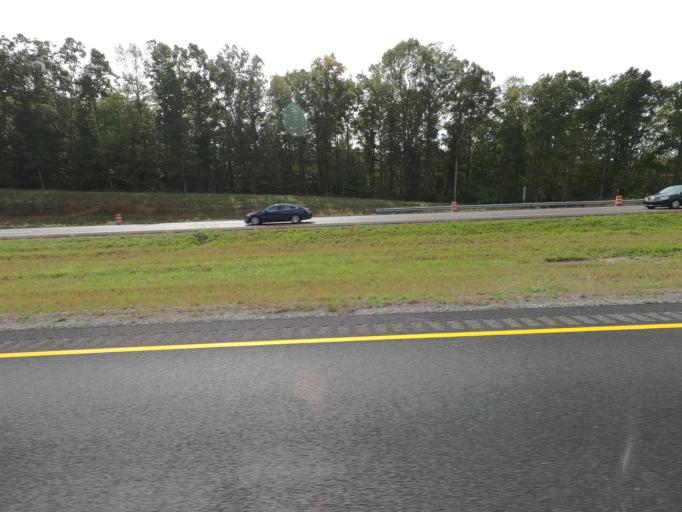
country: US
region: Tennessee
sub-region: Decatur County
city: Parsons
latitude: 35.8201
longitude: -88.1670
